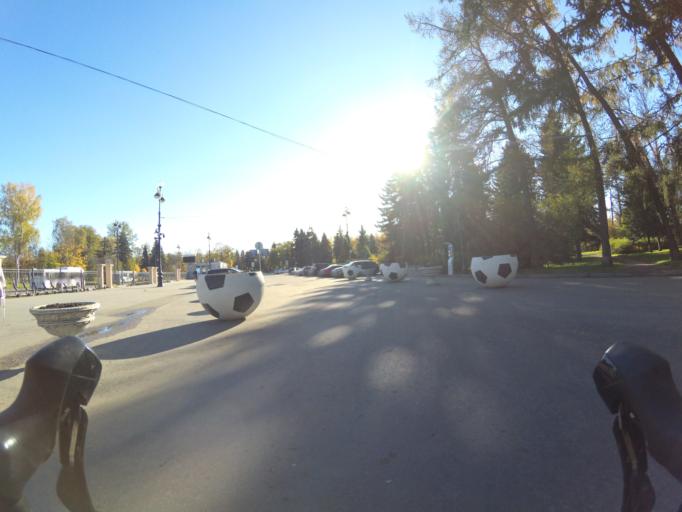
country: RU
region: Leningrad
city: Krestovskiy ostrov
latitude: 59.9696
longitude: 30.2466
